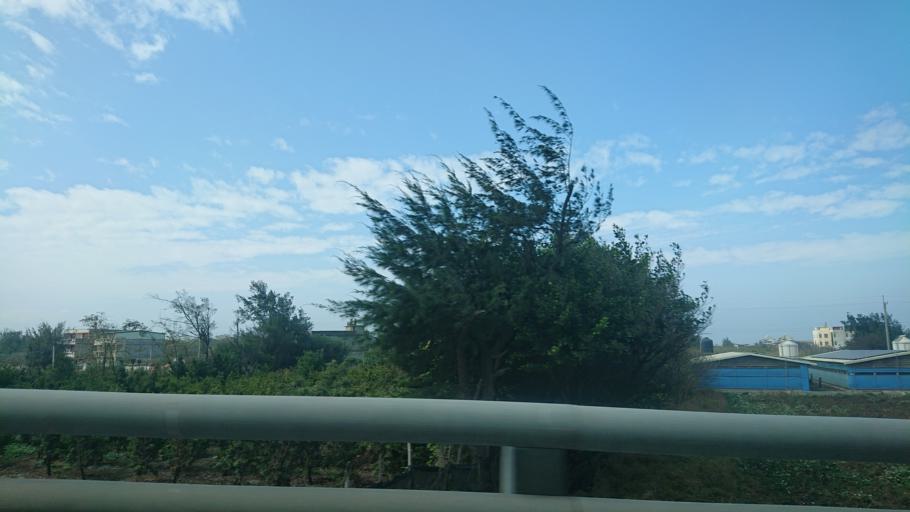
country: TW
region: Taiwan
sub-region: Yunlin
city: Douliu
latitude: 23.8598
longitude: 120.2956
